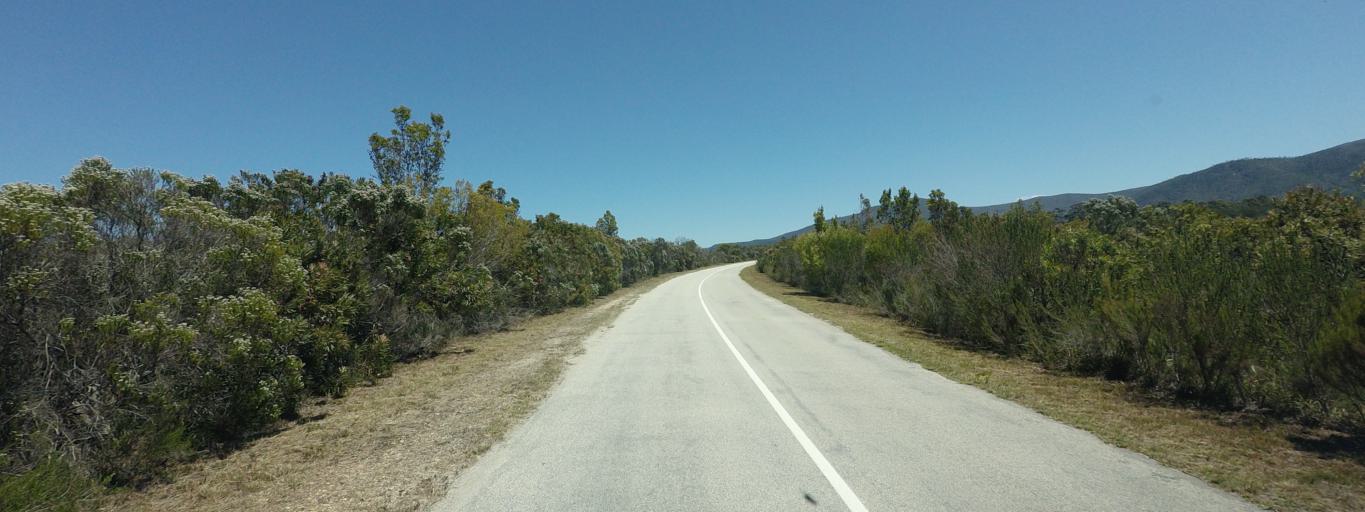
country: ZA
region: Western Cape
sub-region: Eden District Municipality
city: Plettenberg Bay
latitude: -33.9577
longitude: 23.5168
